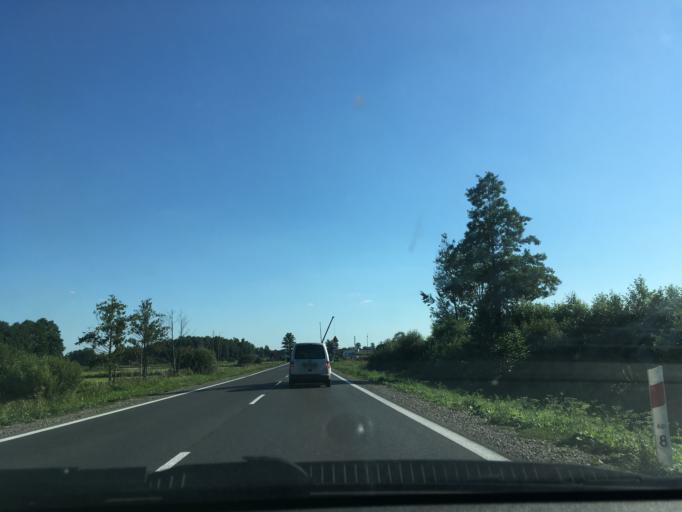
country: PL
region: Podlasie
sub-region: Powiat sokolski
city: Suchowola
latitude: 53.4582
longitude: 23.0882
